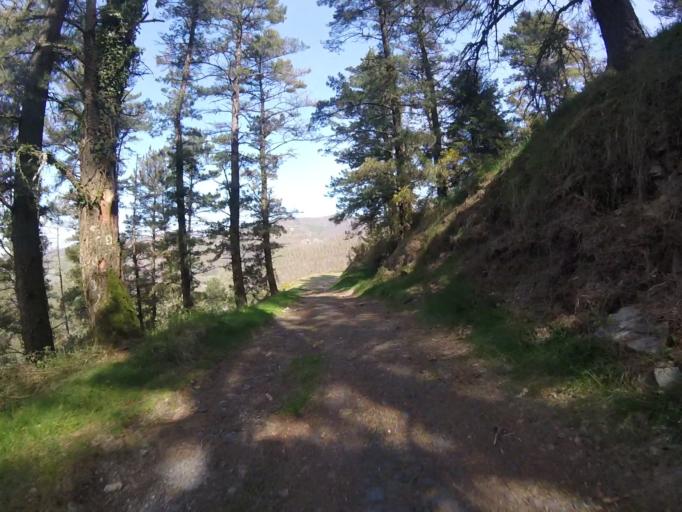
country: ES
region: Basque Country
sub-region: Provincia de Guipuzcoa
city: Irun
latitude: 43.2746
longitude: -1.8060
